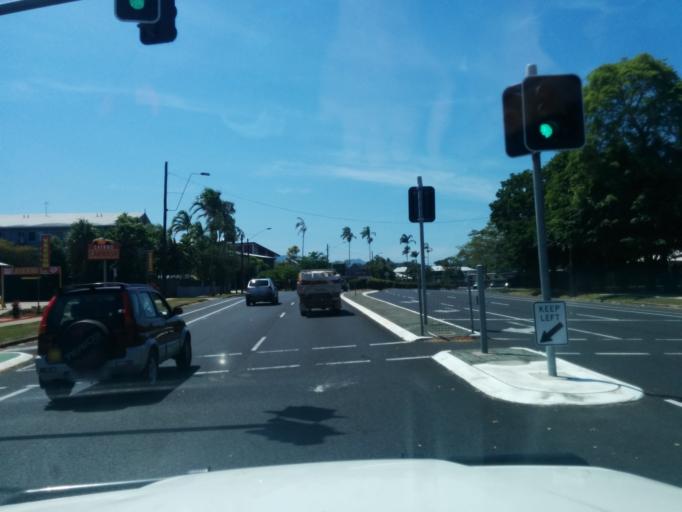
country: AU
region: Queensland
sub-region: Cairns
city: Cairns
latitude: -16.9249
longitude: 145.7407
